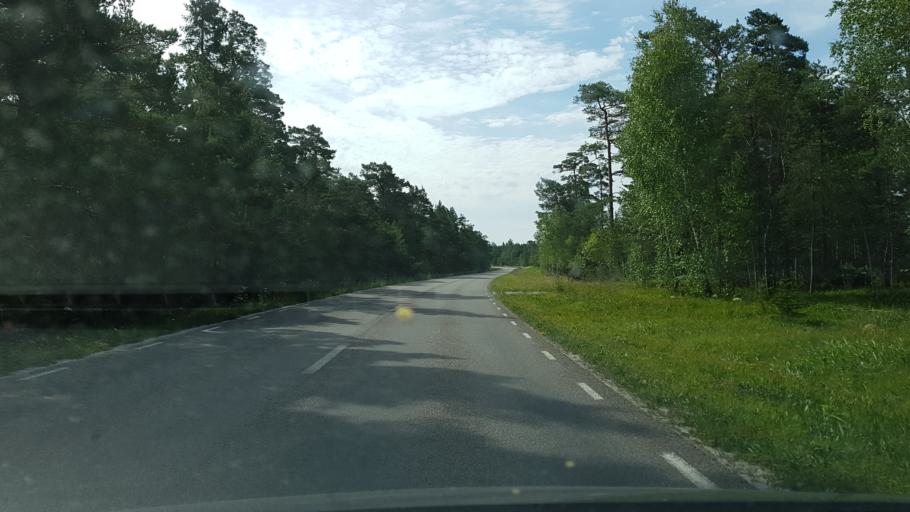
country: SE
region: Gotland
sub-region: Gotland
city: Hemse
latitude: 57.4569
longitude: 18.5768
